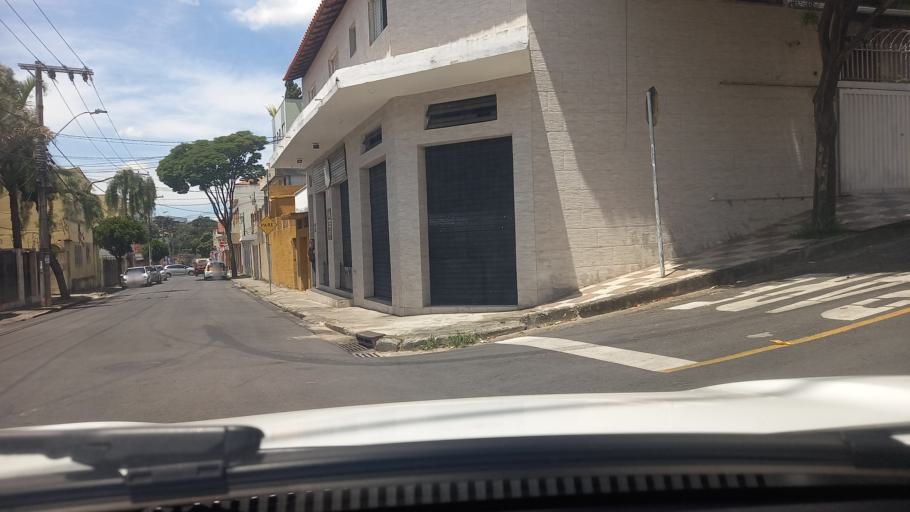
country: BR
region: Minas Gerais
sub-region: Belo Horizonte
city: Belo Horizonte
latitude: -19.9161
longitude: -43.9858
